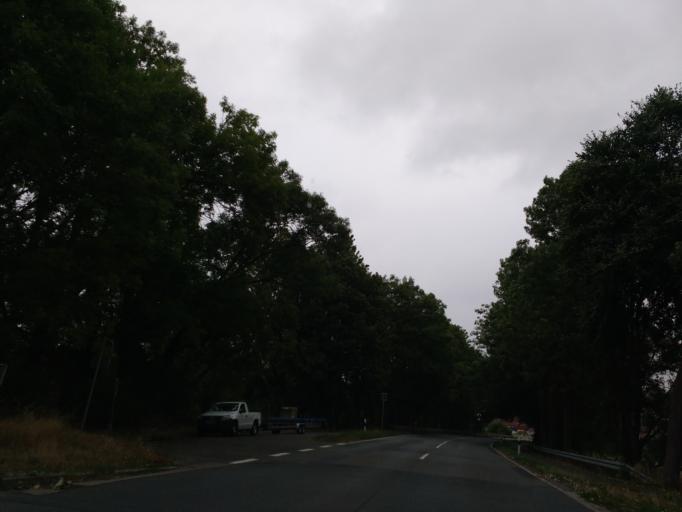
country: DE
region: Lower Saxony
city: Sohlde
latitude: 52.2190
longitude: 10.2161
